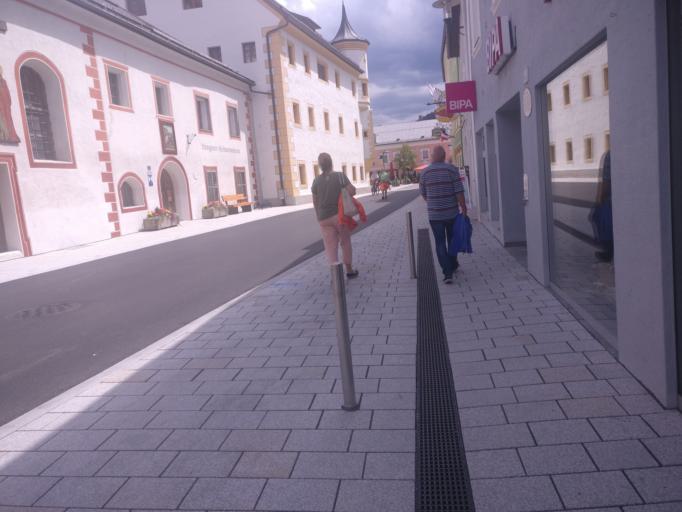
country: AT
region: Salzburg
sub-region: Politischer Bezirk Tamsweg
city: Tamsweg
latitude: 47.1269
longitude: 13.8101
